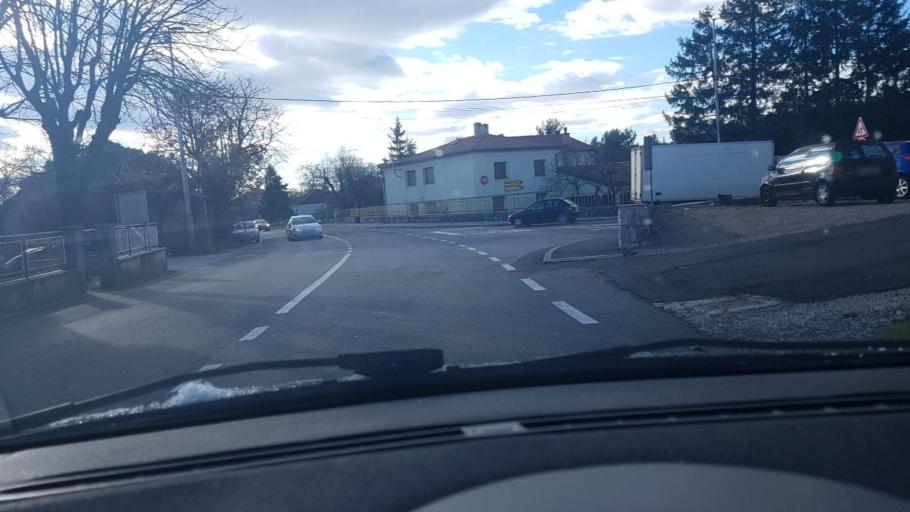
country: HR
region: Primorsko-Goranska
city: Cavle
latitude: 45.3604
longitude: 14.4882
